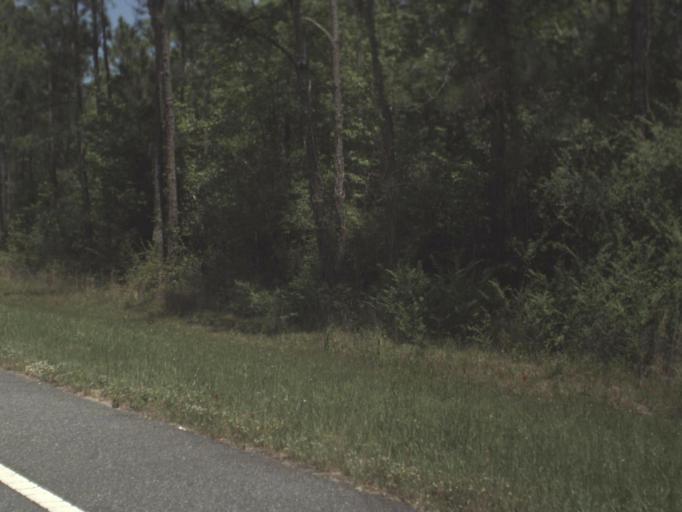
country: US
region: Florida
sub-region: Santa Rosa County
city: Point Baker
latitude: 30.7918
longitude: -87.0414
